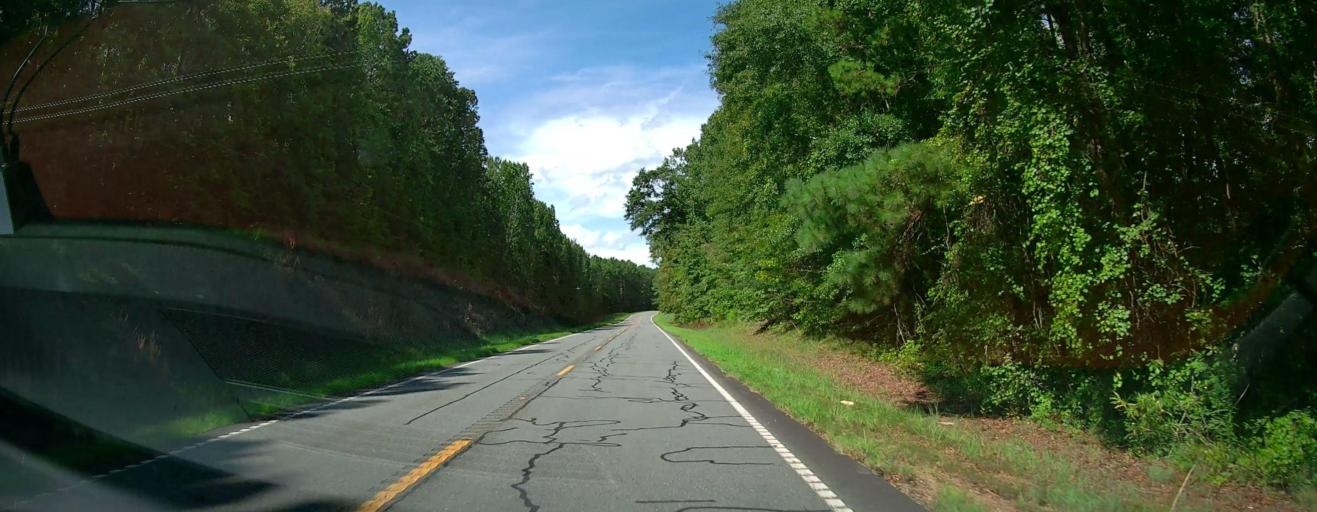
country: US
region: Georgia
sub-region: Talbot County
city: Talbotton
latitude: 32.7130
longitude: -84.5566
